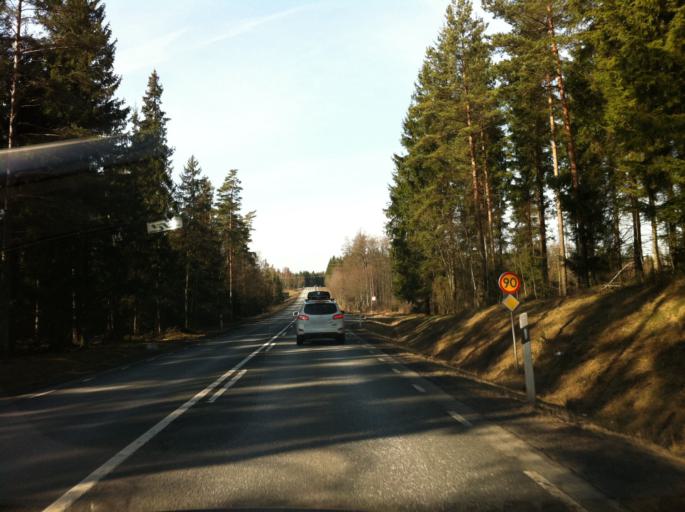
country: SE
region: Joenkoeping
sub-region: Jonkopings Kommun
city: Bankeryd
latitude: 57.8429
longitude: 14.0470
